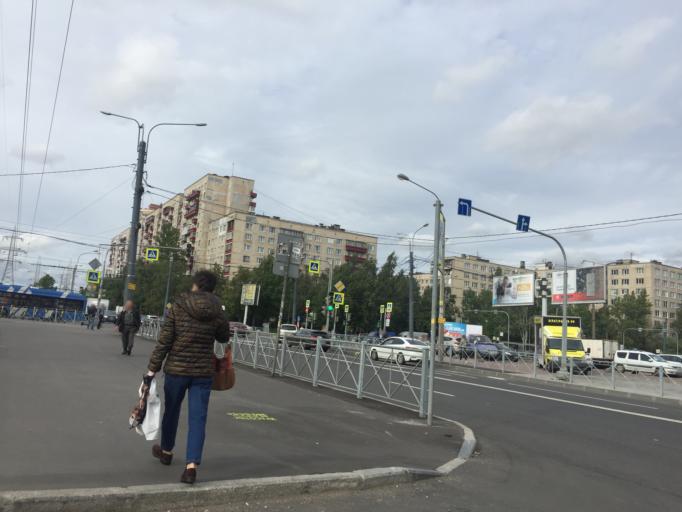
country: RU
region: St.-Petersburg
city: Shushary
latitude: 59.8303
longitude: 30.3839
